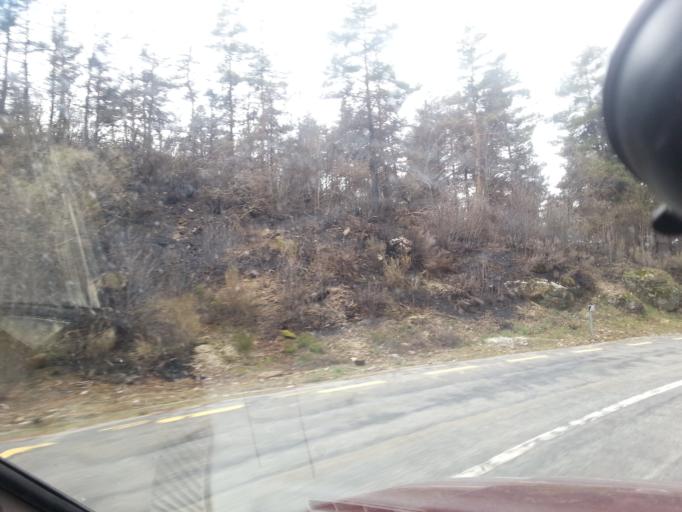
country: PT
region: Guarda
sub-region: Manteigas
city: Manteigas
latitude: 40.4119
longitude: -7.5758
